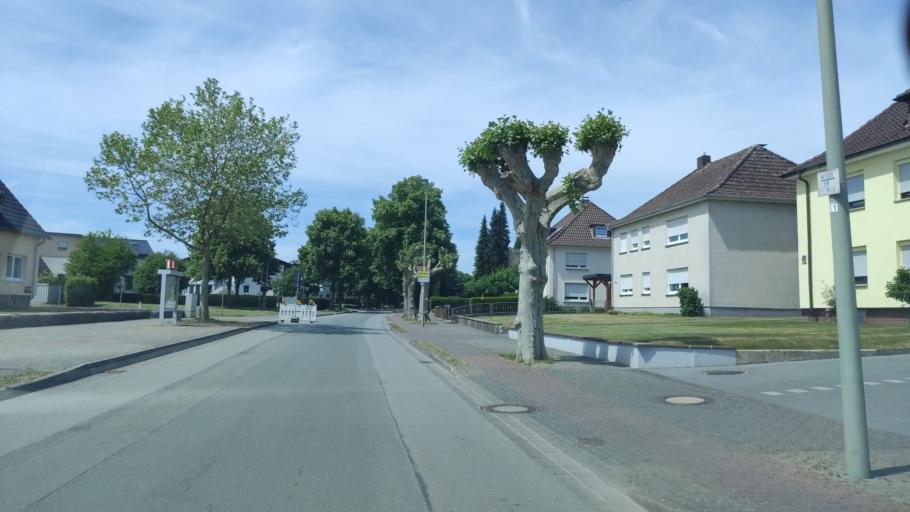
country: DE
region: North Rhine-Westphalia
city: Brakel
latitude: 51.7215
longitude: 9.1756
